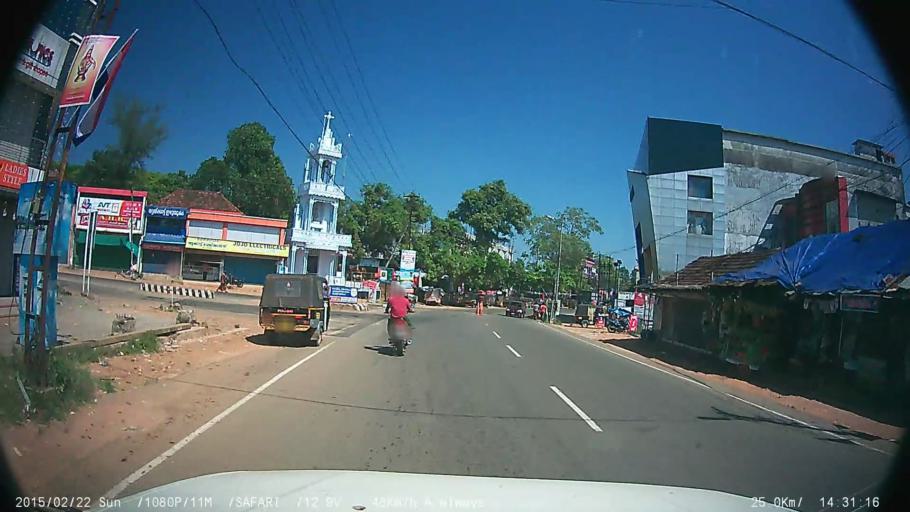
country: IN
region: Kerala
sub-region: Kottayam
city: Erattupetta
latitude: 9.5658
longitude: 76.7540
